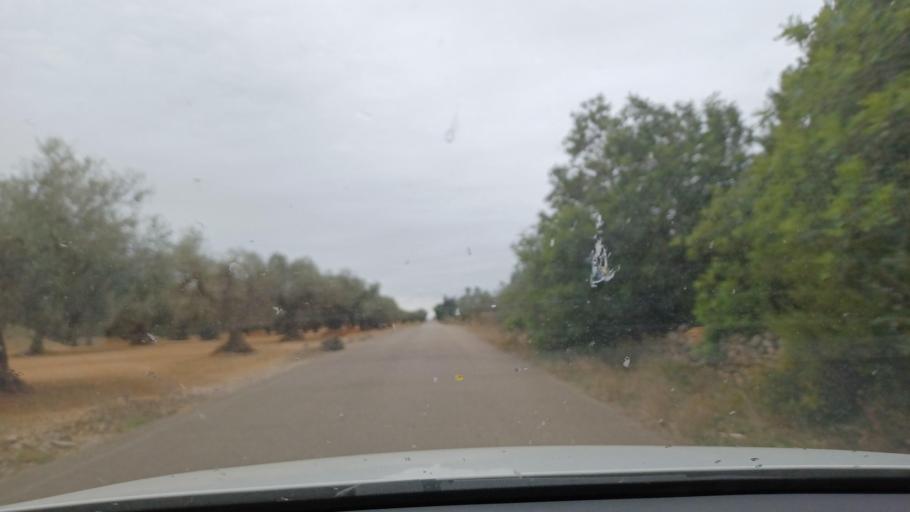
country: ES
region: Valencia
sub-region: Provincia de Castello
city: Canet lo Roig
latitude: 40.5762
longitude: 0.2808
